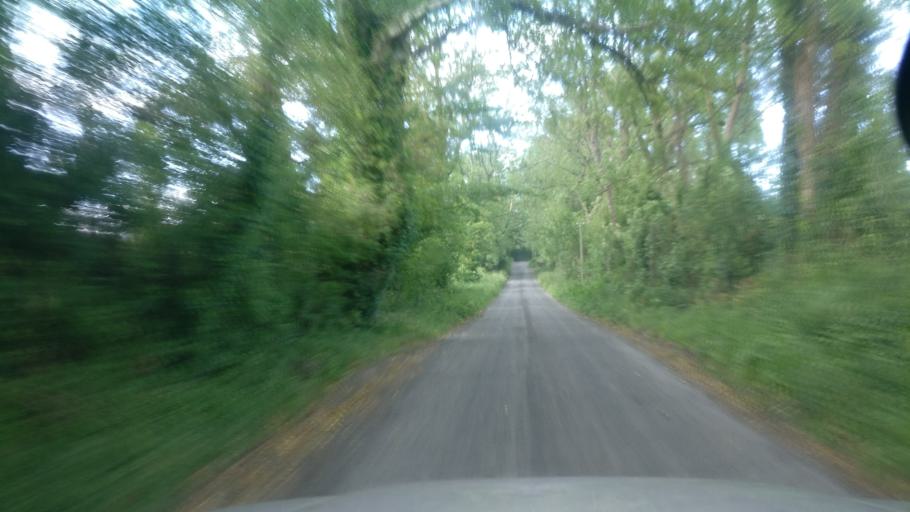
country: IE
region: Connaught
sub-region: County Galway
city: Ballinasloe
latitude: 53.2366
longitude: -8.2303
